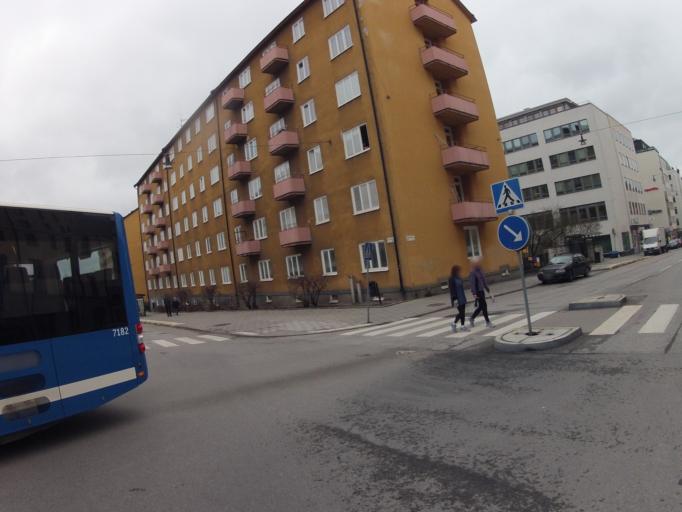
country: SE
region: Stockholm
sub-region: Stockholms Kommun
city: Stockholm
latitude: 59.3486
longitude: 18.0456
